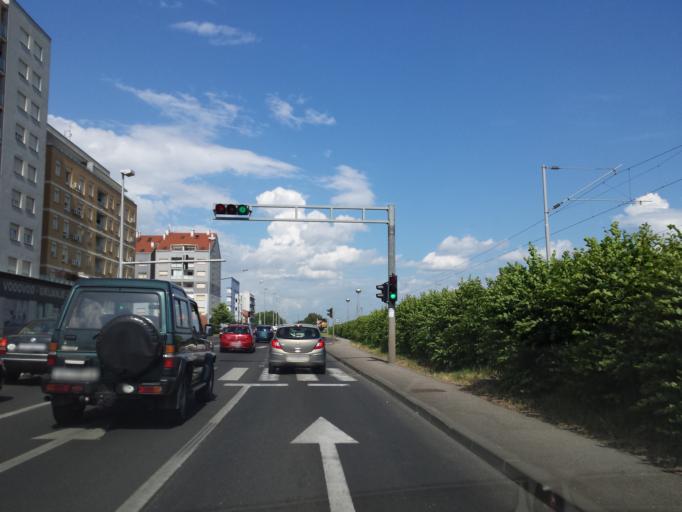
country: HR
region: Grad Zagreb
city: Dubrava
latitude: 45.8146
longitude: 16.0263
